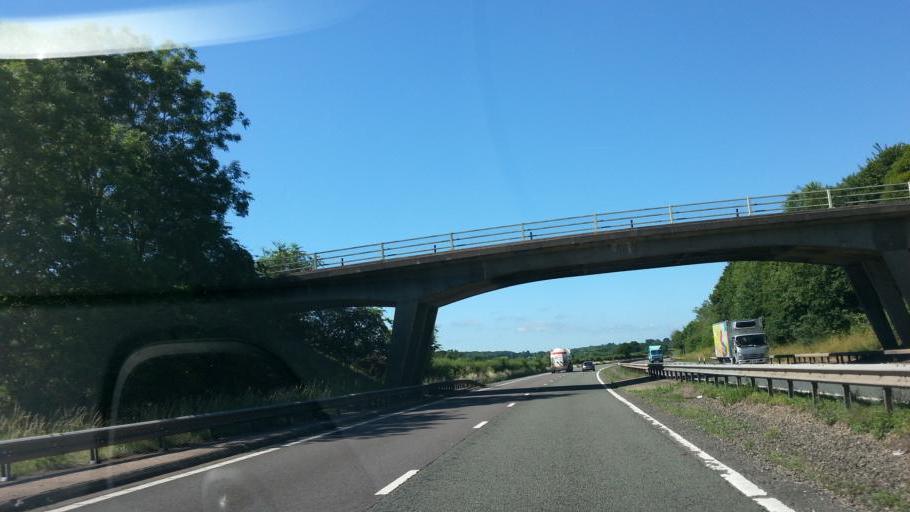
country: GB
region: England
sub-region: Herefordshire
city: Donnington
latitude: 51.9861
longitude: -2.4010
